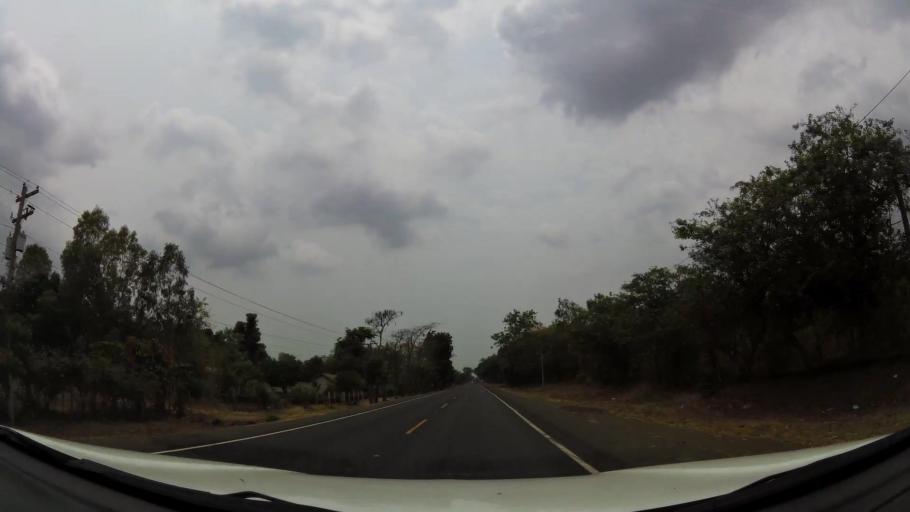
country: NI
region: Leon
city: Telica
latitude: 12.5280
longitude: -86.8835
